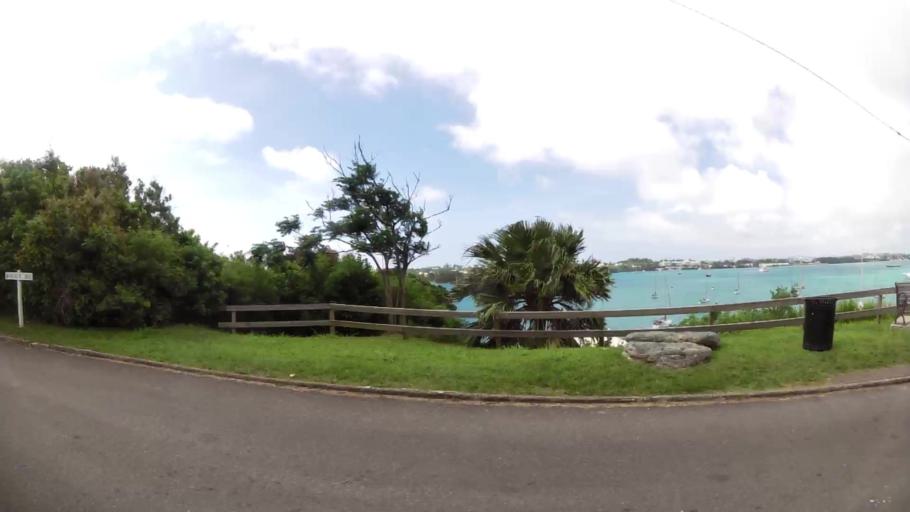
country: BM
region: Saint George
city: Saint George
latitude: 32.3819
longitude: -64.6724
